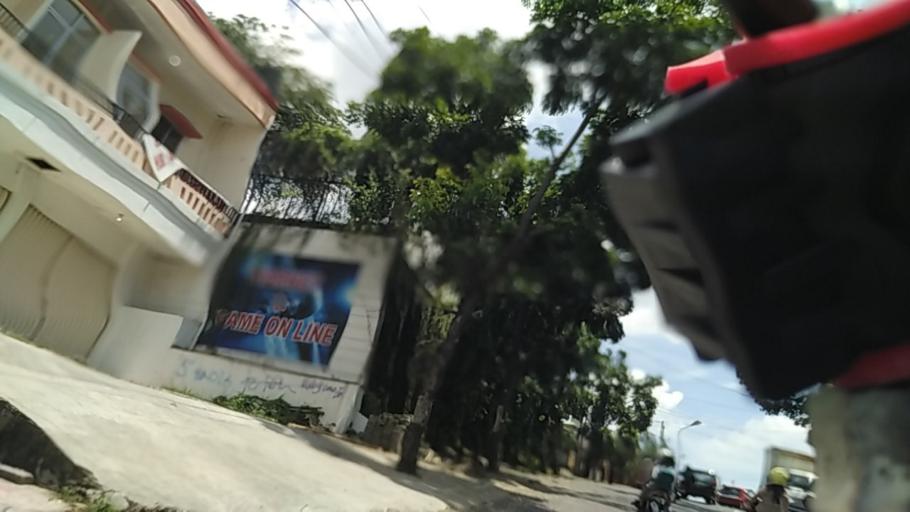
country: ID
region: Central Java
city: Semarang
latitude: -7.0002
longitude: 110.3798
